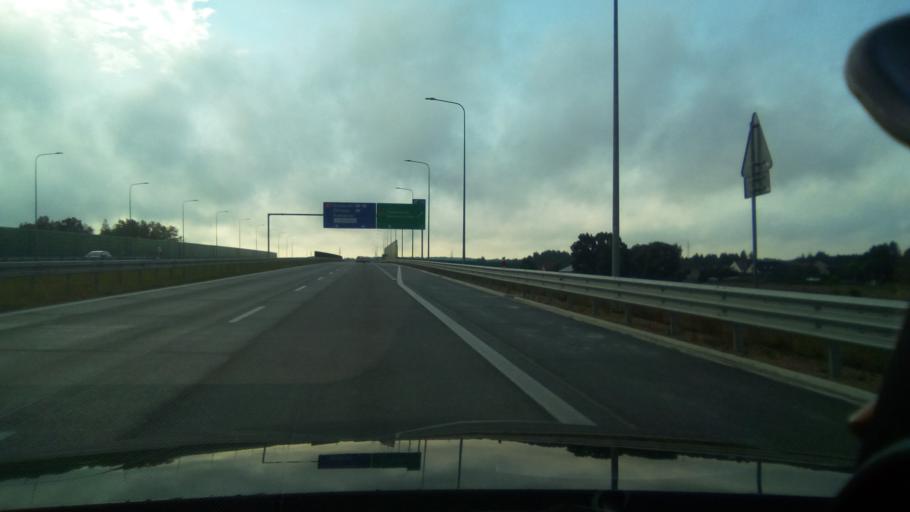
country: PL
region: Silesian Voivodeship
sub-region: Powiat czestochowski
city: Konopiska
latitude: 50.7475
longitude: 19.0393
